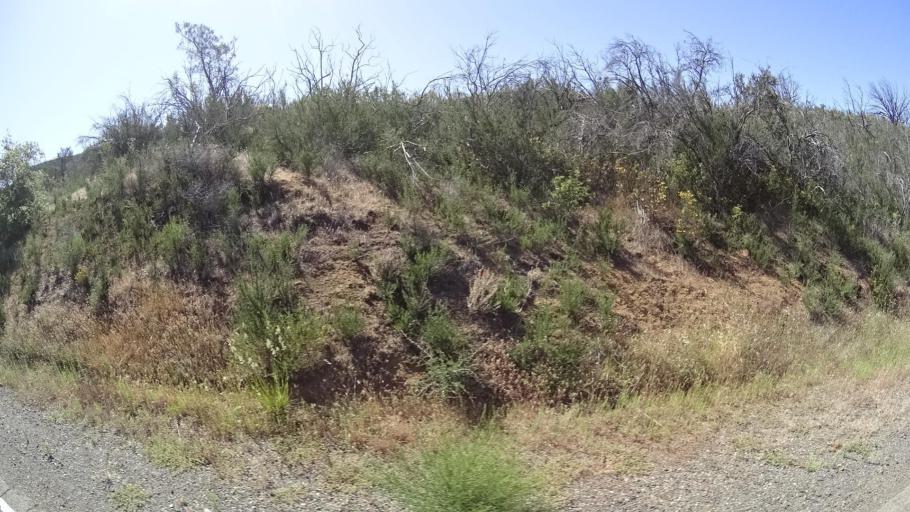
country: US
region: California
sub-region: Lake County
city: Hidden Valley Lake
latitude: 38.8843
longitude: -122.5139
